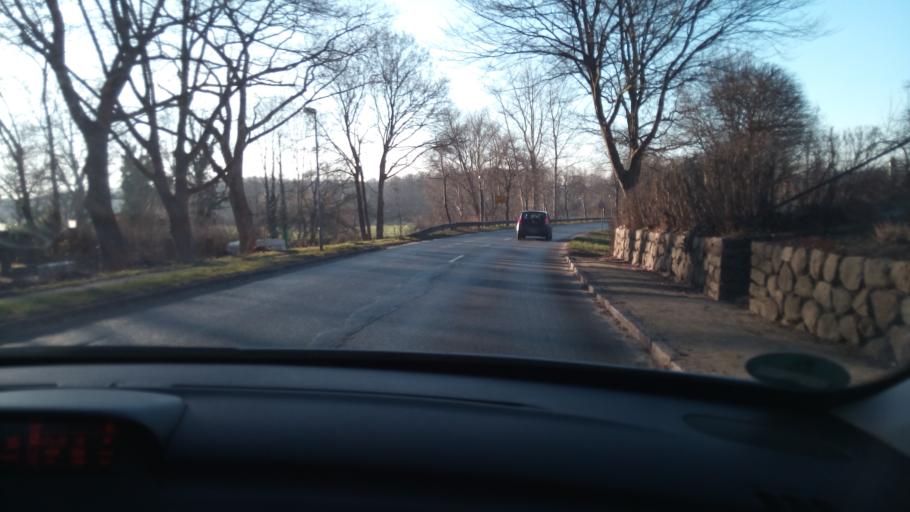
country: DE
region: Schleswig-Holstein
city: Fitzen
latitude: 53.4803
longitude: 10.6380
